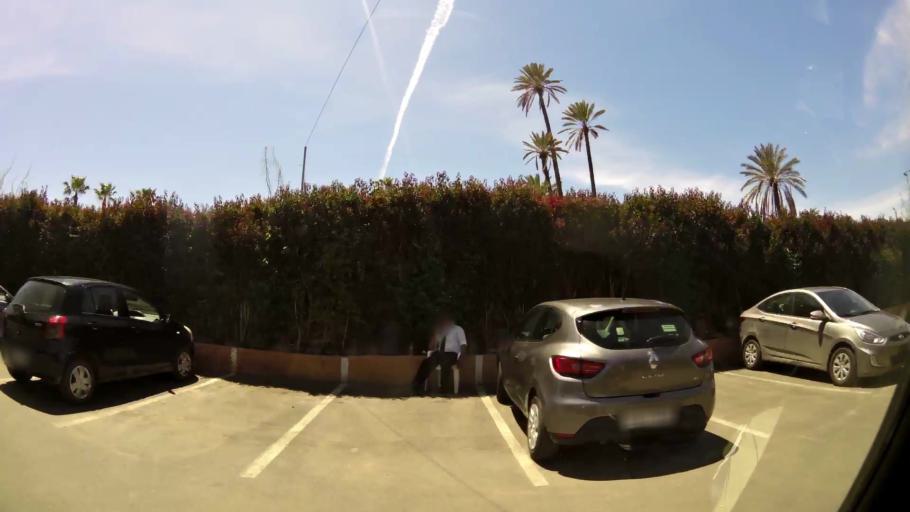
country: MA
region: Marrakech-Tensift-Al Haouz
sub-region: Marrakech
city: Marrakesh
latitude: 31.6232
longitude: -7.9972
